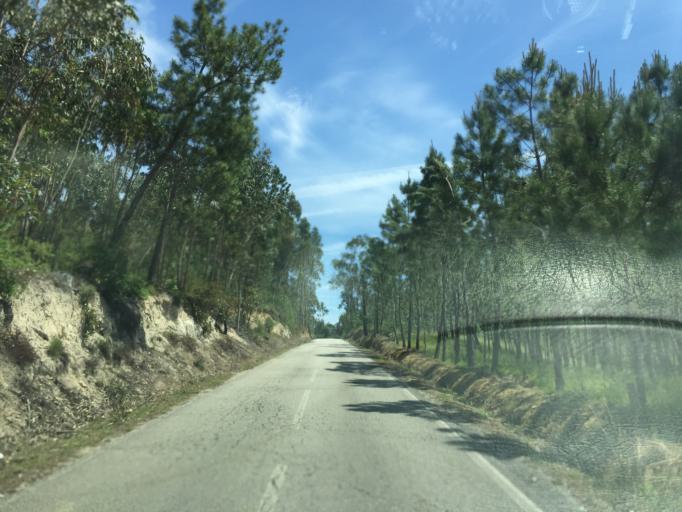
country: PT
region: Leiria
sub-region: Pombal
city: Lourical
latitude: 40.0660
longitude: -8.7230
